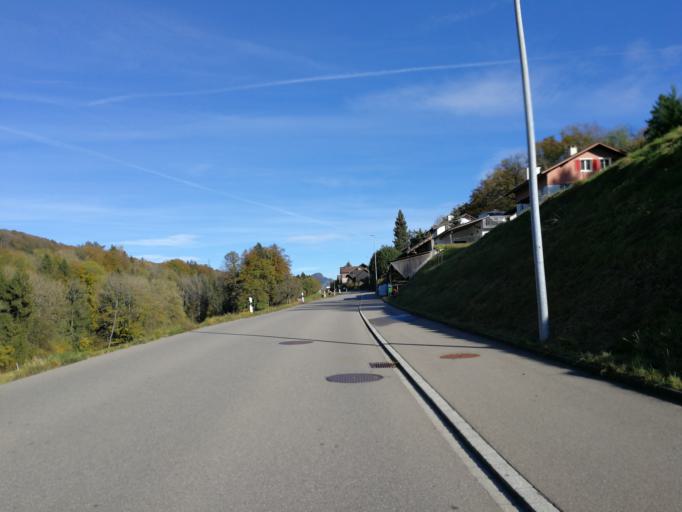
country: CH
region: Zurich
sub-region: Bezirk Hinwil
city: Rueti / Oberdorf
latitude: 47.2463
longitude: 8.8890
